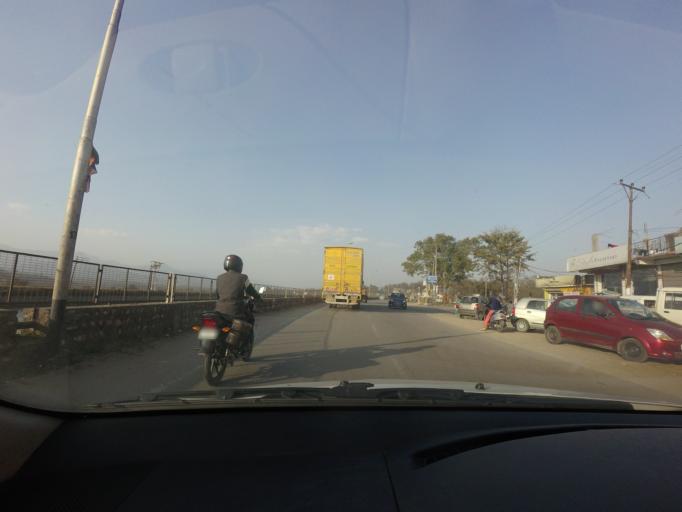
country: IN
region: Himachal Pradesh
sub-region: Mandi
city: Sundarnagar
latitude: 31.5433
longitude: 76.8972
